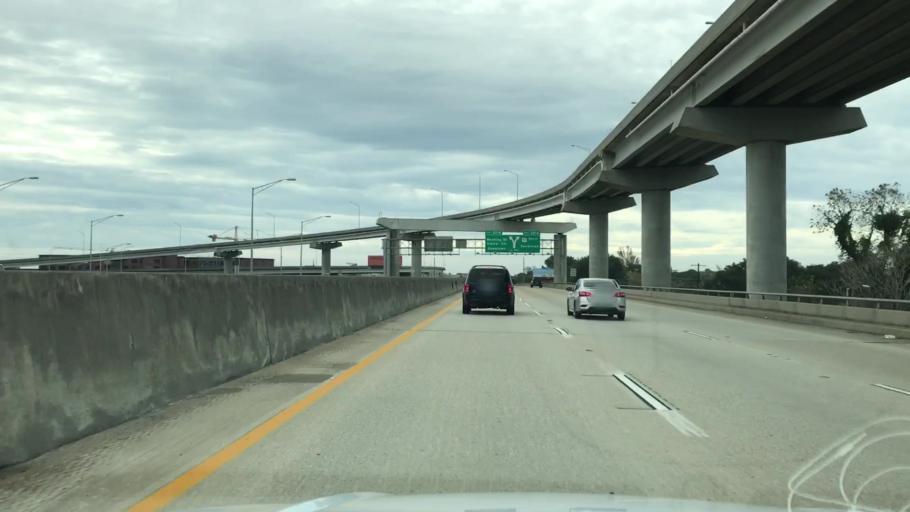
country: US
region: South Carolina
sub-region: Charleston County
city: Charleston
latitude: 32.8058
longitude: -79.9486
